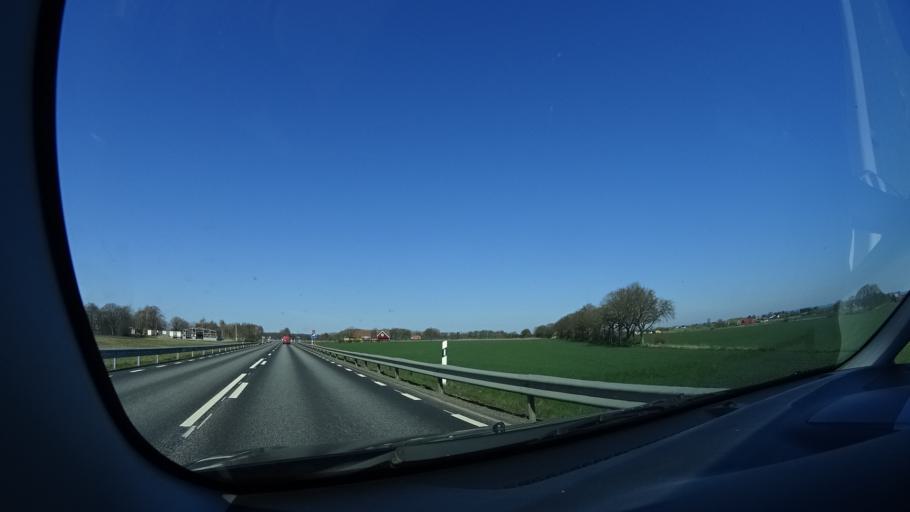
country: SE
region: Skane
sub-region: Angelholms Kommun
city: Strovelstorp
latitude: 56.2041
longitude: 12.7825
